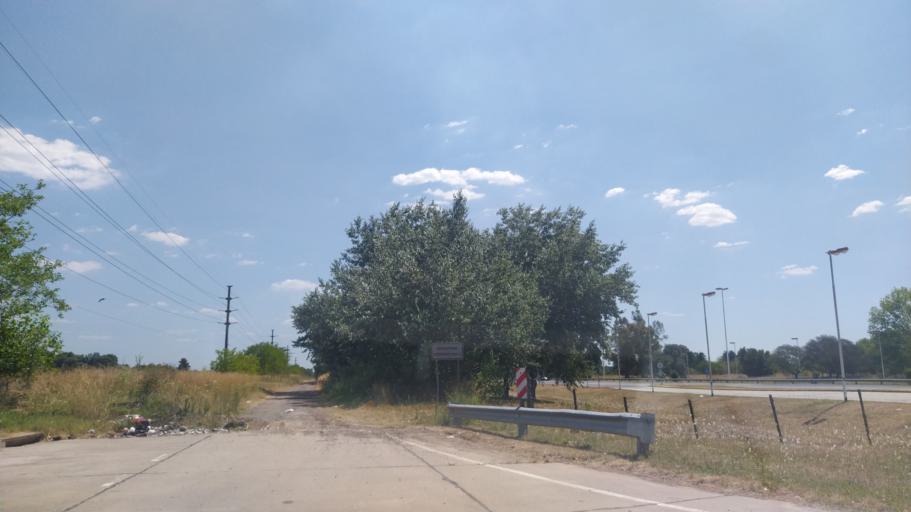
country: AR
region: Buenos Aires
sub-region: Partido de Ezeiza
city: Ezeiza
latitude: -34.9065
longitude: -58.6218
